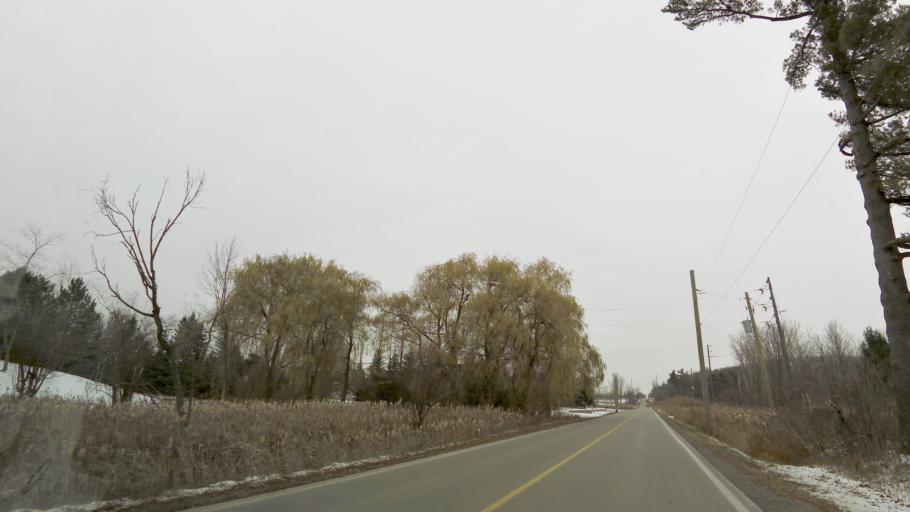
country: CA
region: Ontario
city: Vaughan
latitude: 43.8716
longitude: -79.5937
